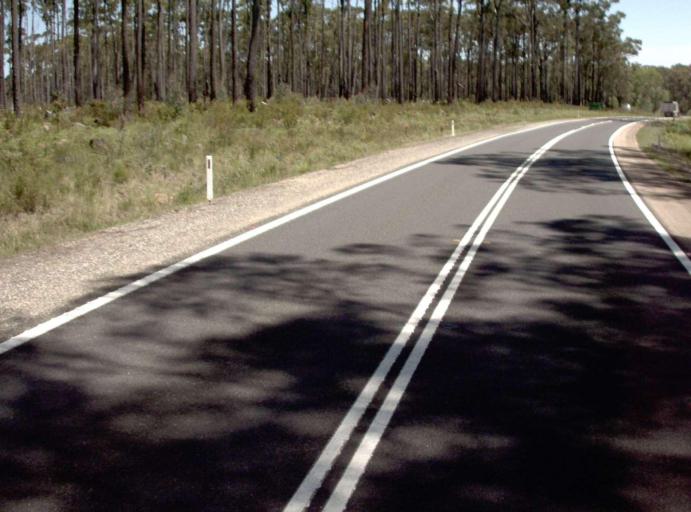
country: AU
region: Victoria
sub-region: East Gippsland
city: Lakes Entrance
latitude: -37.6695
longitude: 148.7984
